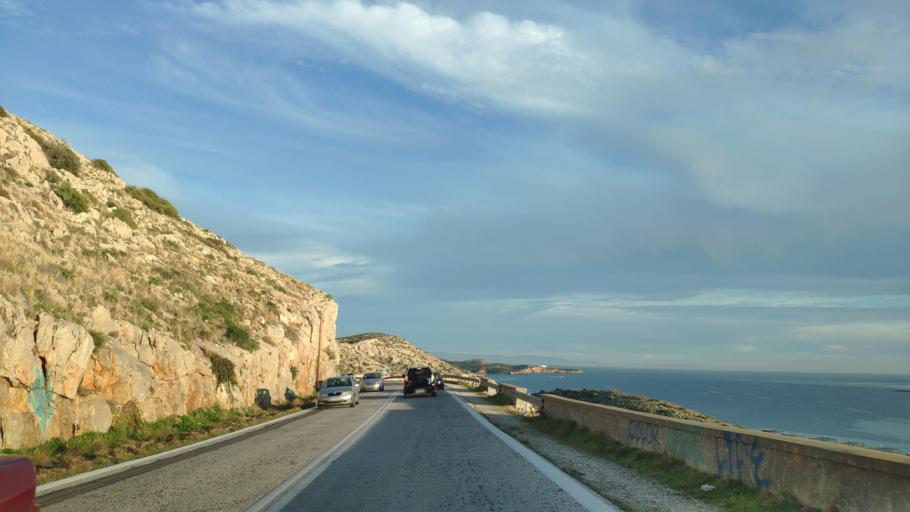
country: GR
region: Attica
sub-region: Nomarchia Anatolikis Attikis
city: Palaia Fokaia
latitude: 37.6712
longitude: 23.9418
